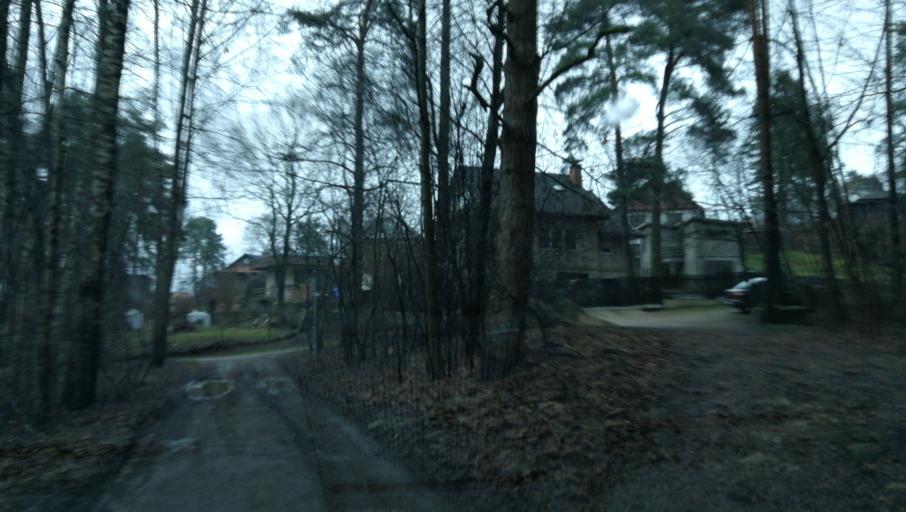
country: LV
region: Riga
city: Jaunciems
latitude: 56.9939
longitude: 24.2232
